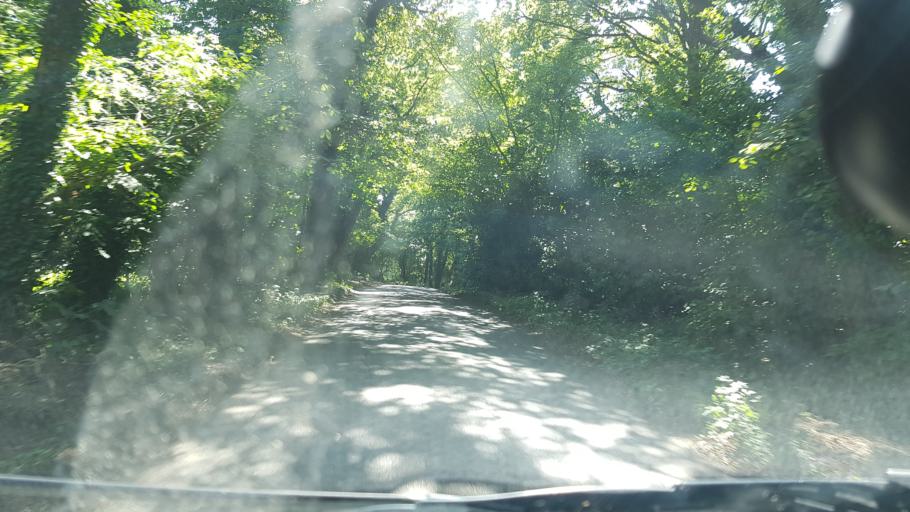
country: GB
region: England
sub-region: Surrey
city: Cranleigh
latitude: 51.1671
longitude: -0.4899
